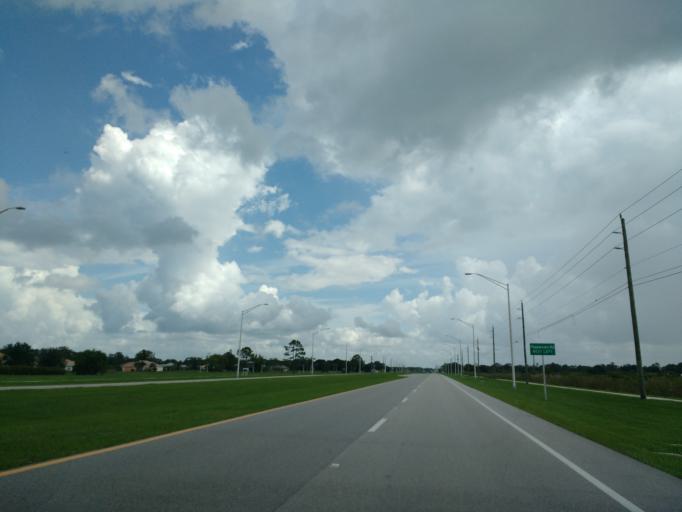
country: US
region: Florida
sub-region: Lee County
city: Burnt Store Marina
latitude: 26.7772
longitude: -82.0378
